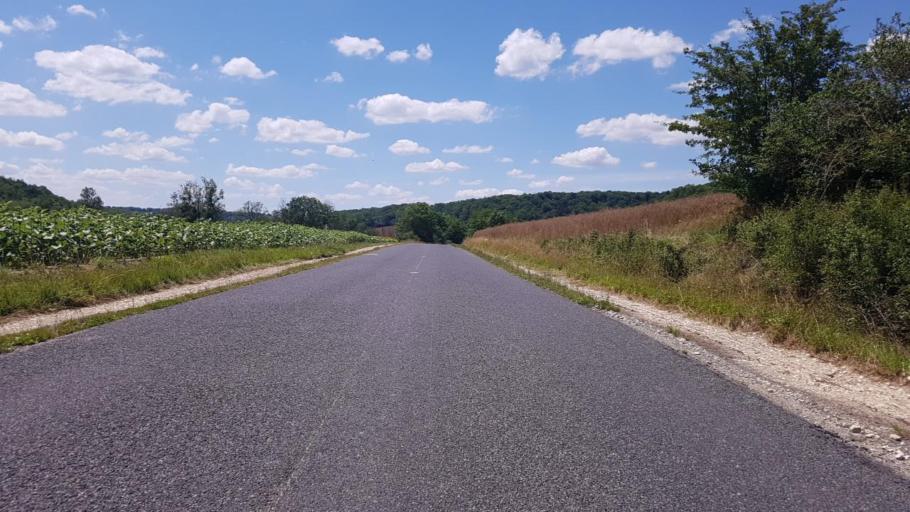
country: FR
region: Lorraine
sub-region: Departement de la Meuse
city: Ligny-en-Barrois
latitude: 48.6473
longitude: 5.4086
